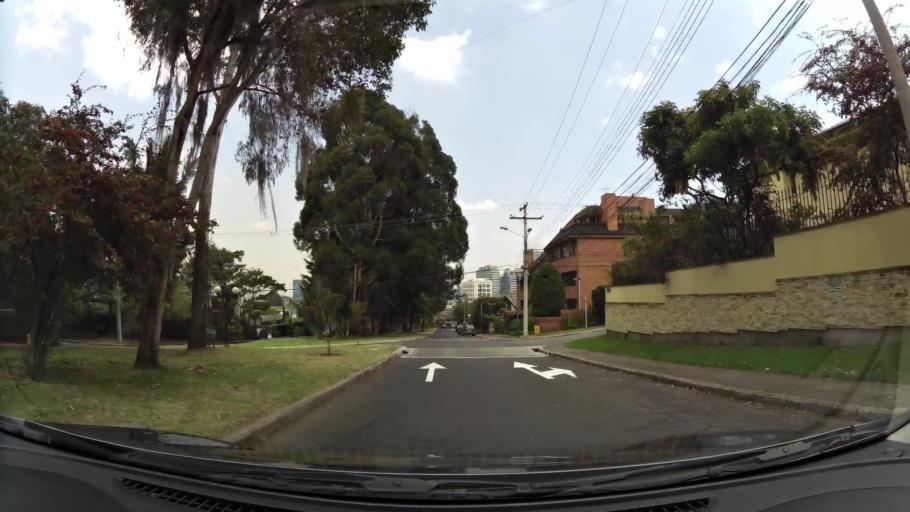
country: CO
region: Bogota D.C.
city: Barrio San Luis
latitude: 4.6866
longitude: -74.0299
